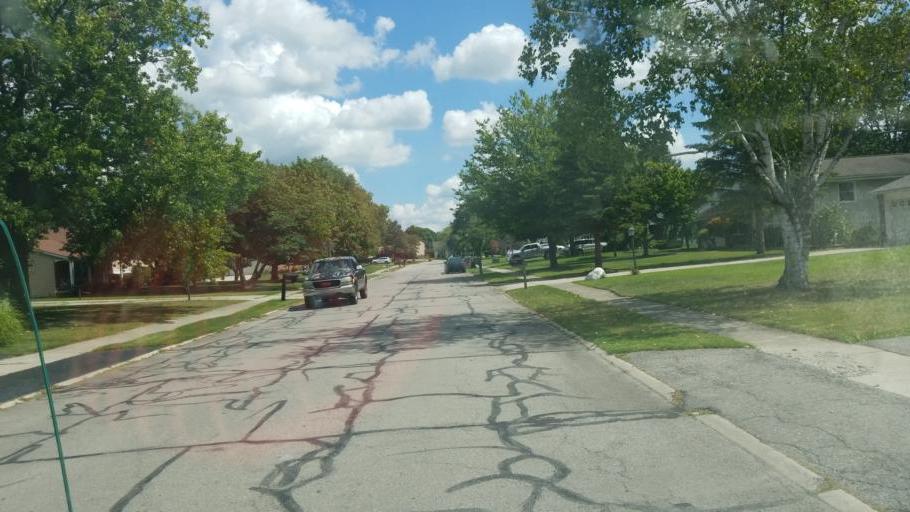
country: US
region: Ohio
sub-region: Marion County
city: Marion
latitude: 40.5708
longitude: -83.0995
